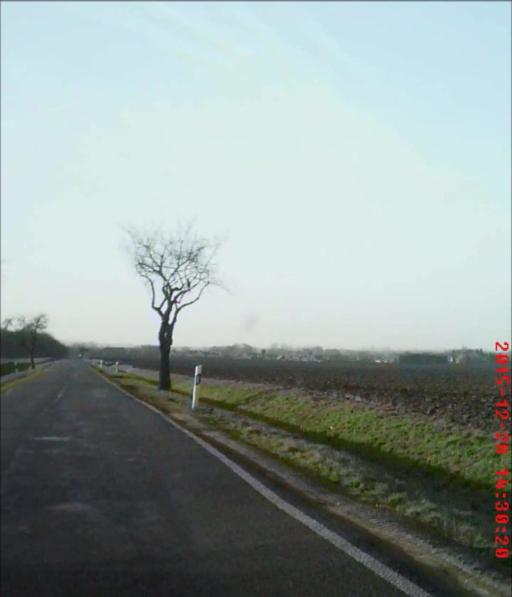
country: DE
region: Thuringia
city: Liebstedt
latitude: 51.0450
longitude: 11.3882
